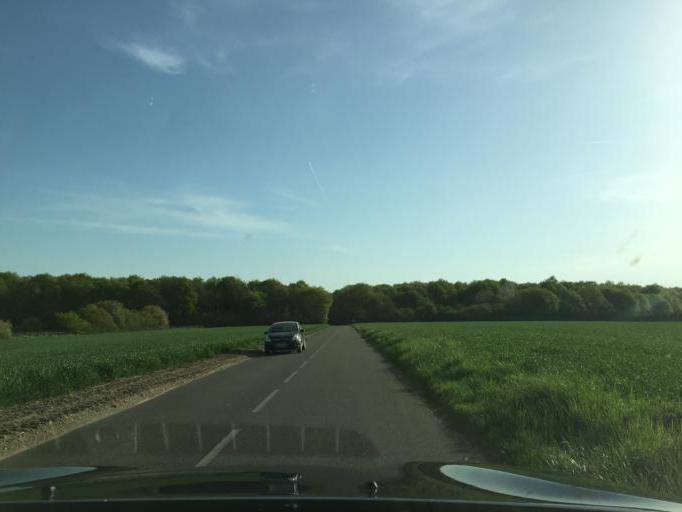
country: FR
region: Ile-de-France
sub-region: Departement des Yvelines
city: Conde-sur-Vesgre
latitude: 48.7282
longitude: 1.6581
